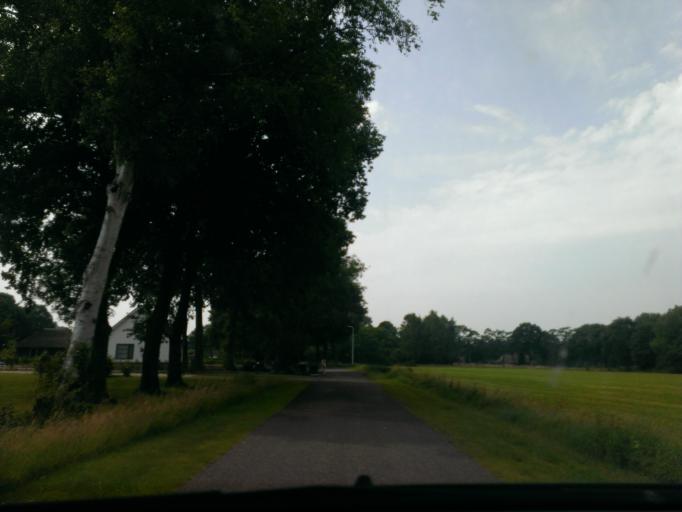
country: NL
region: Overijssel
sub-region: Gemeente Hof van Twente
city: Markelo
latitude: 52.3443
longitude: 6.4714
